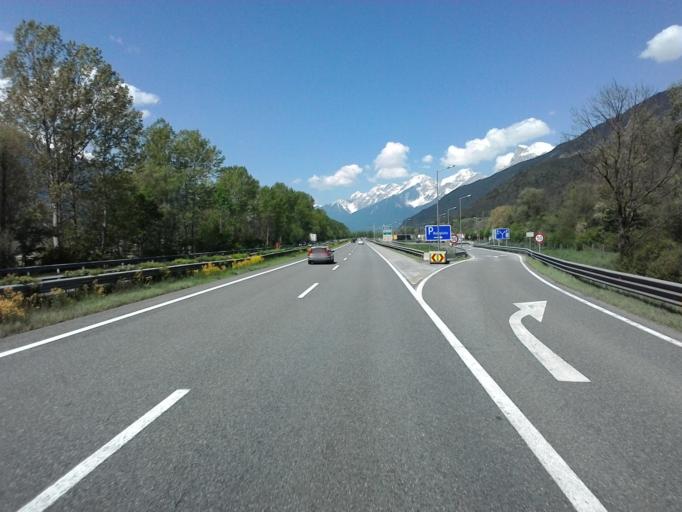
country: AT
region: Tyrol
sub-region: Politischer Bezirk Innsbruck Land
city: Zirl
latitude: 47.2753
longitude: 11.2171
